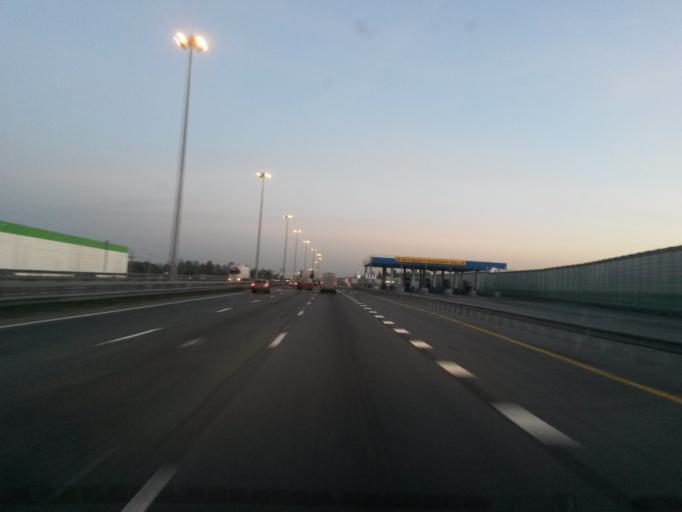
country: RU
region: Moskovskaya
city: Belyye Stolby
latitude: 55.3266
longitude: 37.8106
